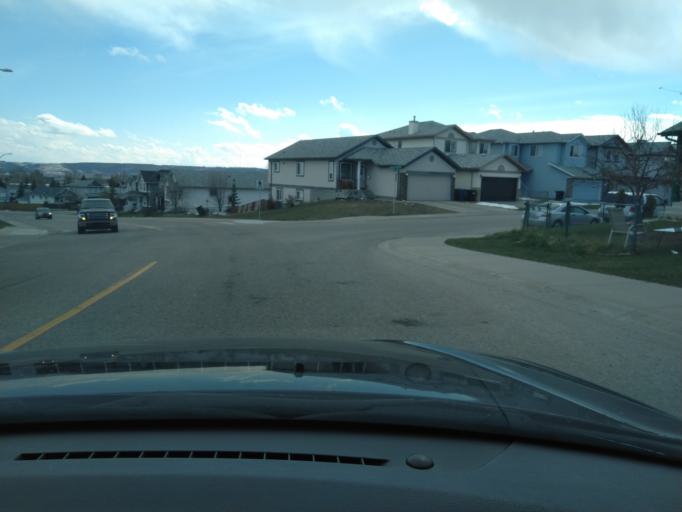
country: CA
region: Alberta
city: Calgary
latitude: 51.1330
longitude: -114.2180
